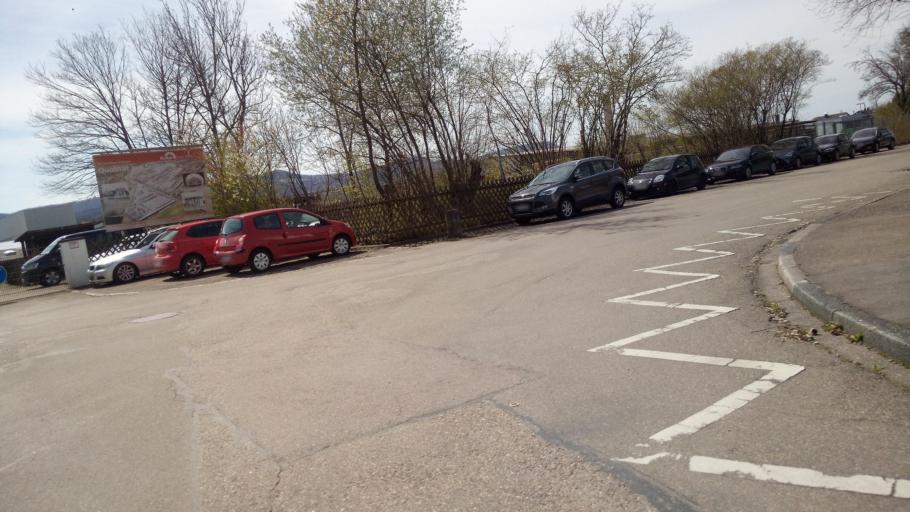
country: DE
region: Baden-Wuerttemberg
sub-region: Regierungsbezirk Stuttgart
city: Sussen
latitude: 48.6853
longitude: 9.7727
